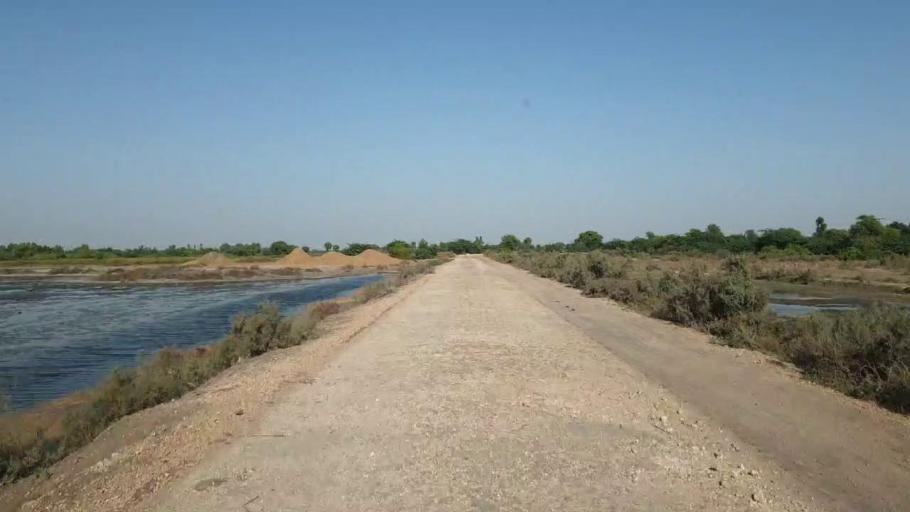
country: PK
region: Sindh
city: Badin
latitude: 24.6011
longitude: 68.9126
